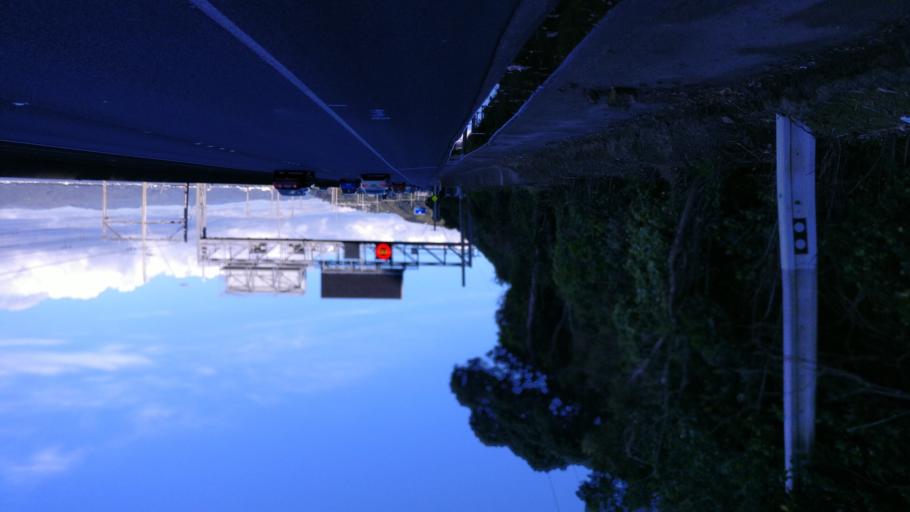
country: NZ
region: Wellington
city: Petone
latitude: -41.2370
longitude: 174.8309
